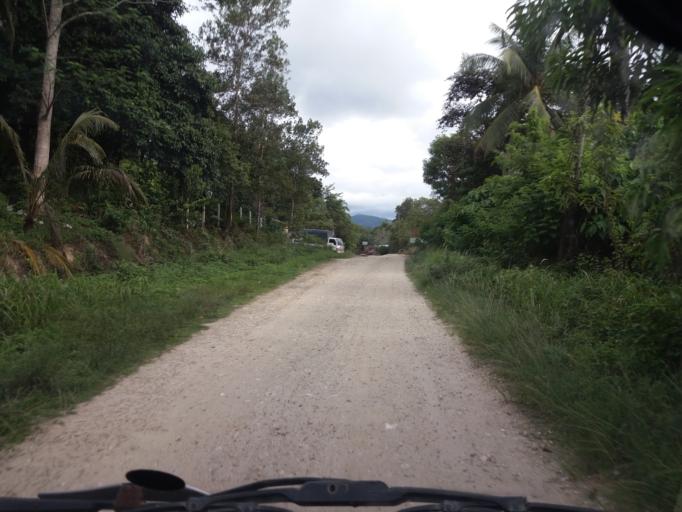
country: PH
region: Mimaropa
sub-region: Province of Palawan
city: San Vicente
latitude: 10.5194
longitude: 119.2711
